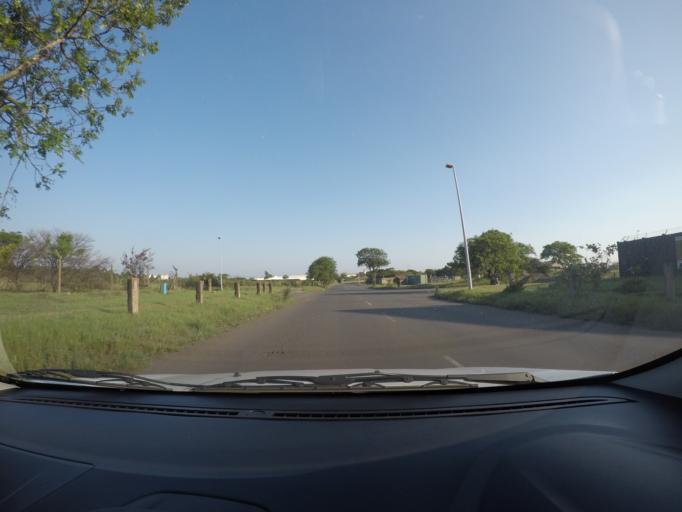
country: ZA
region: KwaZulu-Natal
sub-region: uThungulu District Municipality
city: Richards Bay
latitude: -28.7651
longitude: 32.0085
